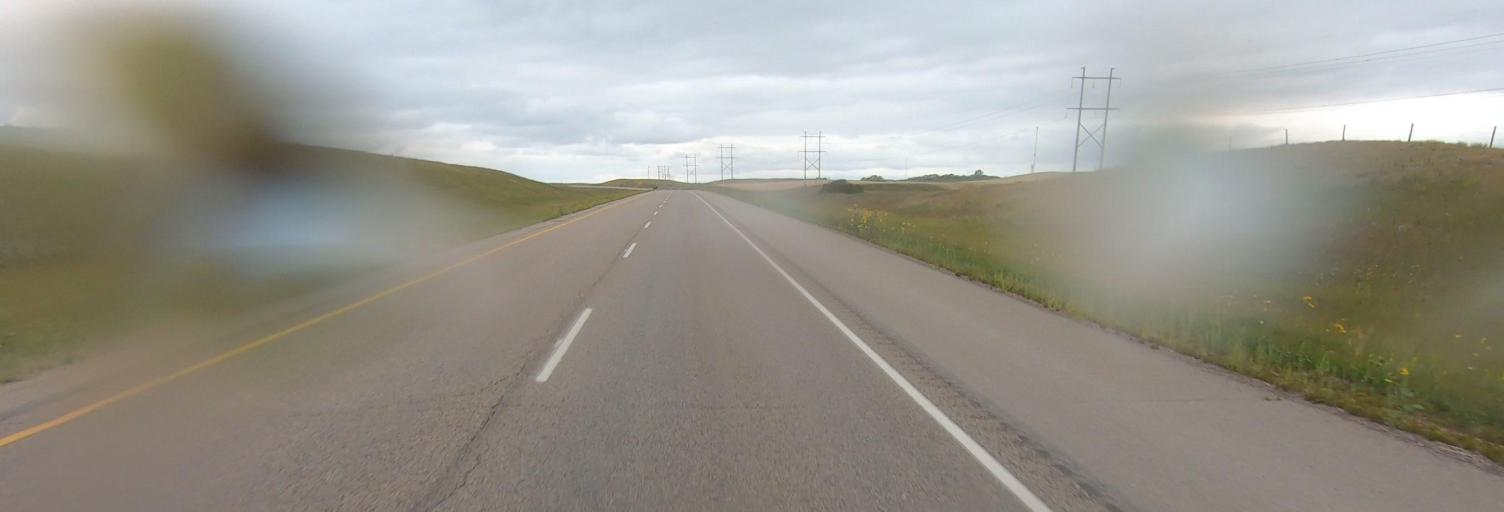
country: CA
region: Saskatchewan
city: Gravelbourg
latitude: 50.4630
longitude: -106.4423
